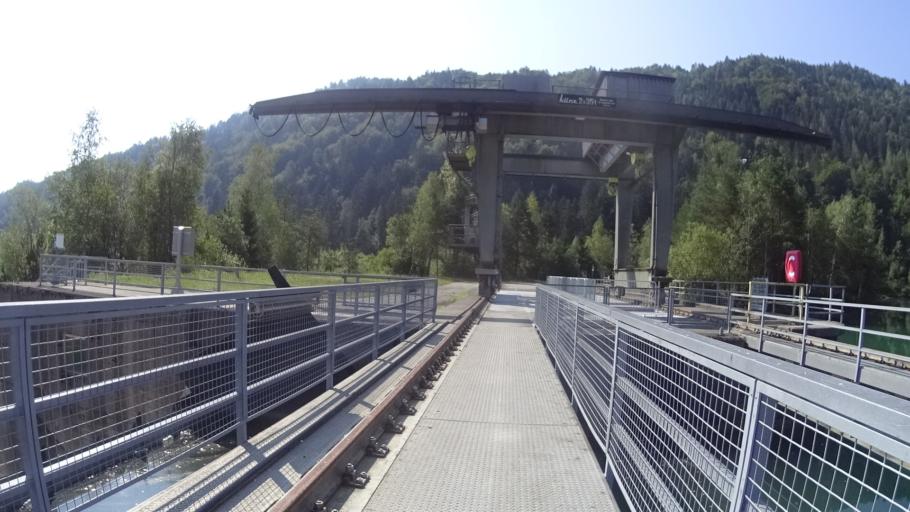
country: AT
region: Carinthia
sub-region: Politischer Bezirk Volkermarkt
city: Gallizien
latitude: 46.5606
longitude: 14.4795
